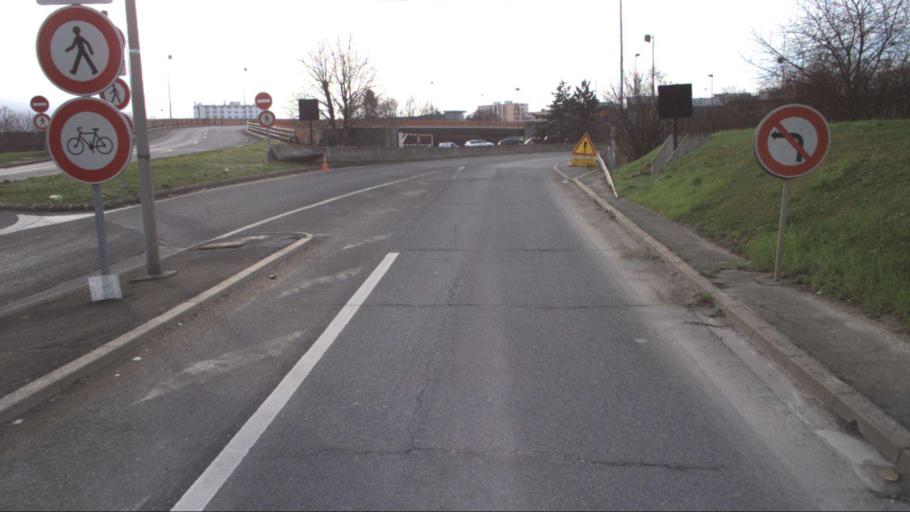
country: FR
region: Ile-de-France
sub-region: Departement du Val-de-Marne
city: Villiers-sur-Marne
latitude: 48.8378
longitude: 2.5430
